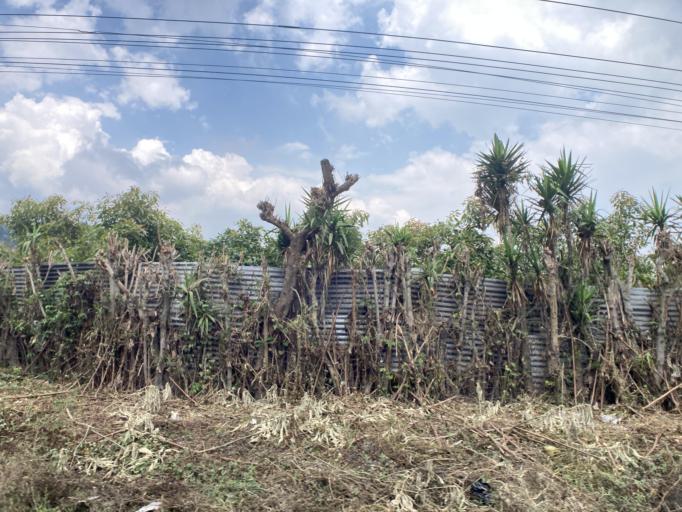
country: GT
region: Guatemala
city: Villa Canales
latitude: 14.4125
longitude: -90.5343
